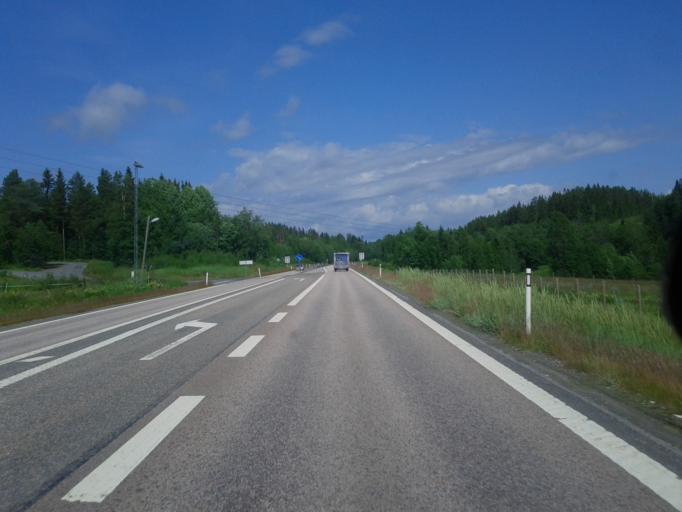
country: SE
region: Vaesternorrland
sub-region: OErnskoeldsviks Kommun
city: Husum
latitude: 63.4187
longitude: 19.2053
